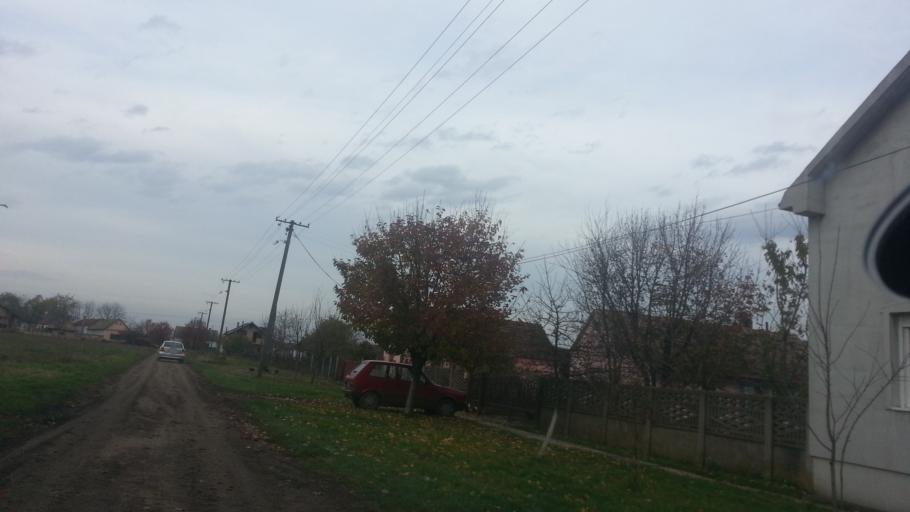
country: RS
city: Putinci
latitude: 44.9645
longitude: 19.9677
